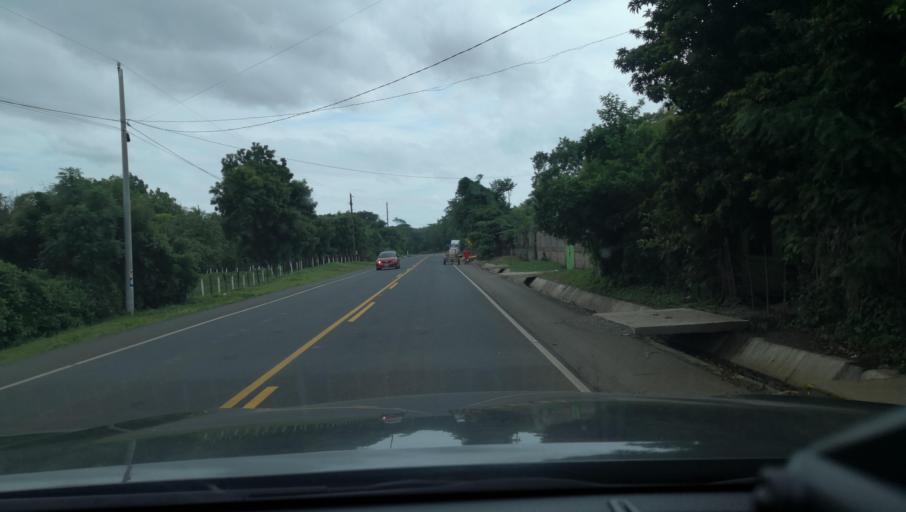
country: NI
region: Masaya
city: Nindiri
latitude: 12.0624
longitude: -86.1386
